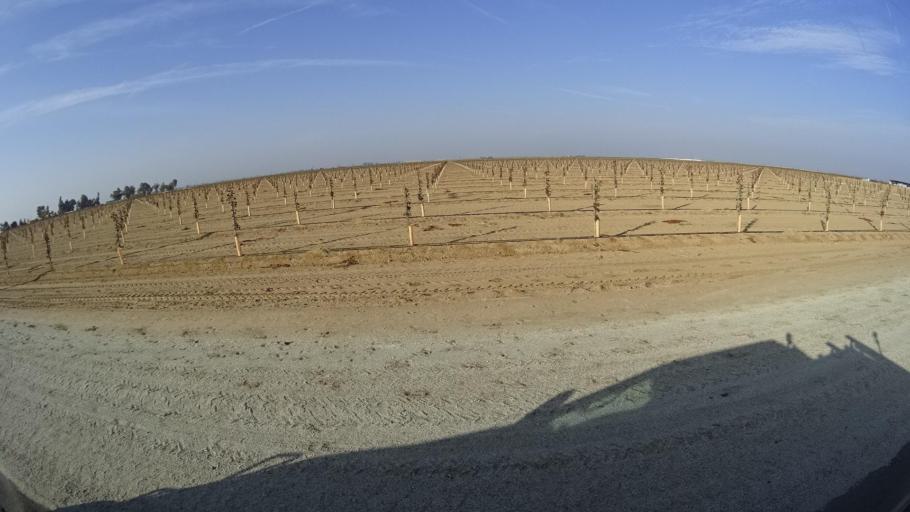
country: US
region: California
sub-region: Kern County
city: McFarland
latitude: 35.6941
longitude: -119.1871
